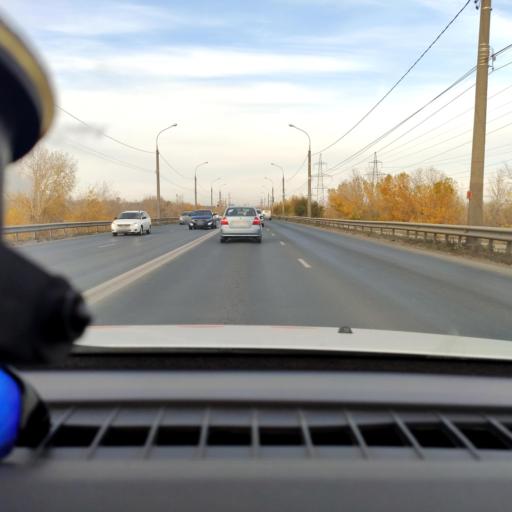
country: RU
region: Samara
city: Samara
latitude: 53.1585
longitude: 50.1933
